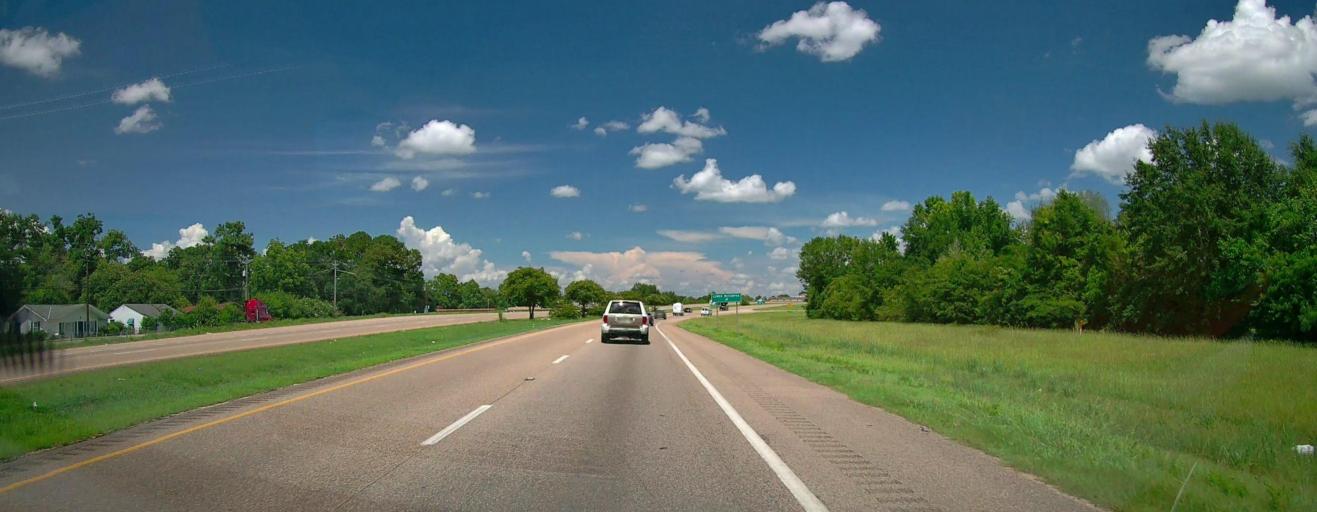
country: US
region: Alabama
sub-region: Montgomery County
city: Montgomery
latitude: 32.4222
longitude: -86.2889
